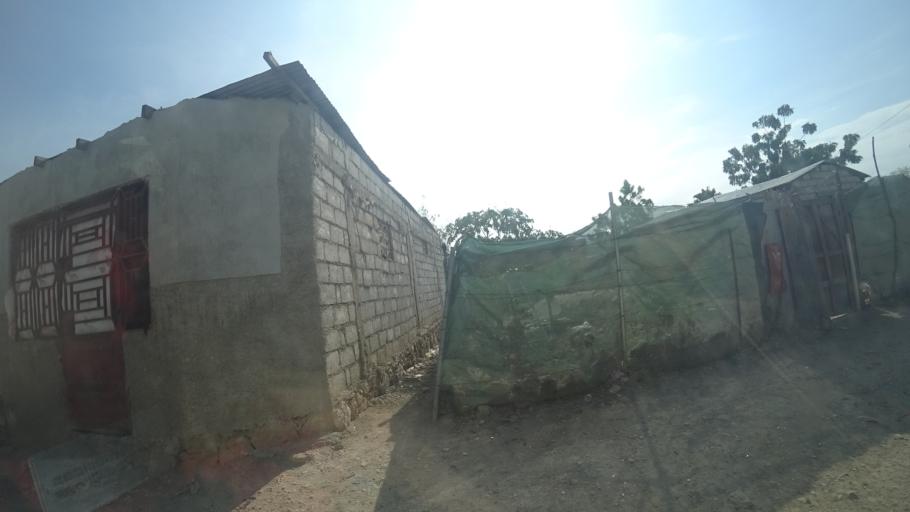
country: HT
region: Ouest
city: Croix des Bouquets
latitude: 18.6572
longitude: -72.2847
